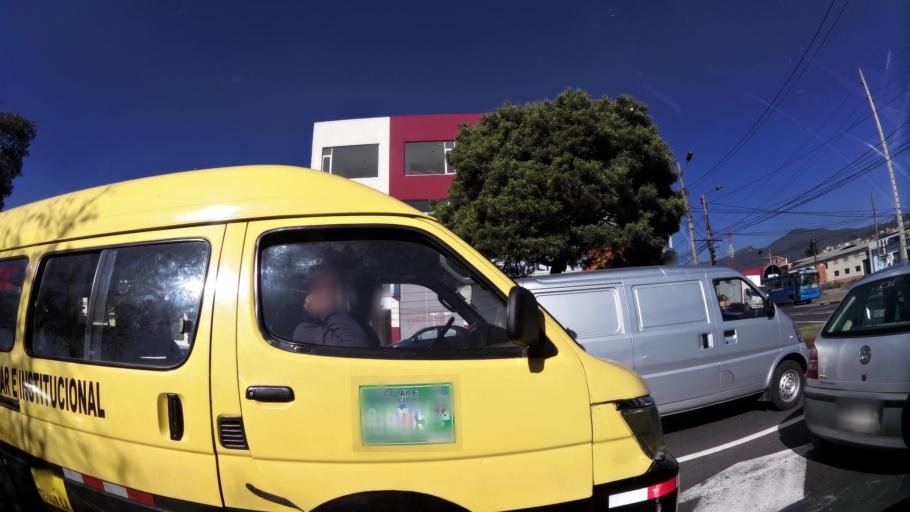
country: EC
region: Pichincha
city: Quito
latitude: -0.2493
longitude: -78.5364
